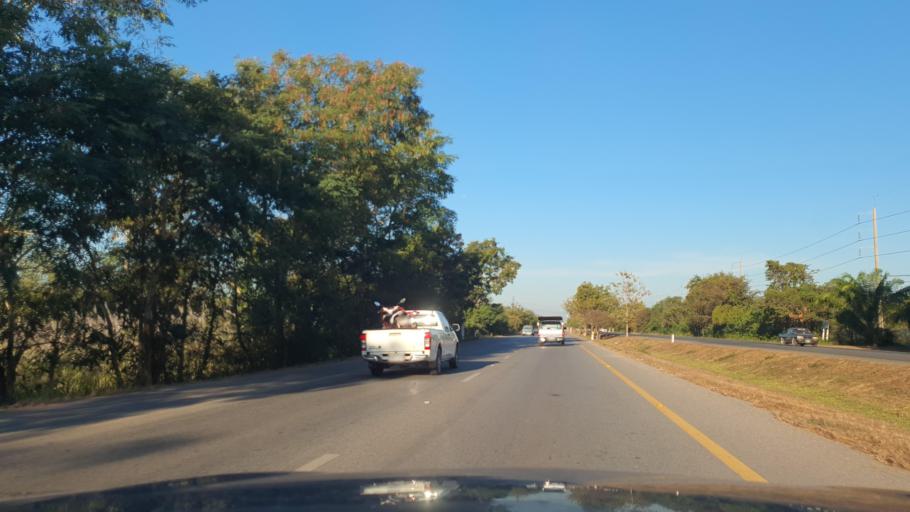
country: TH
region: Phitsanulok
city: Phitsanulok
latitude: 16.8508
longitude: 100.3338
